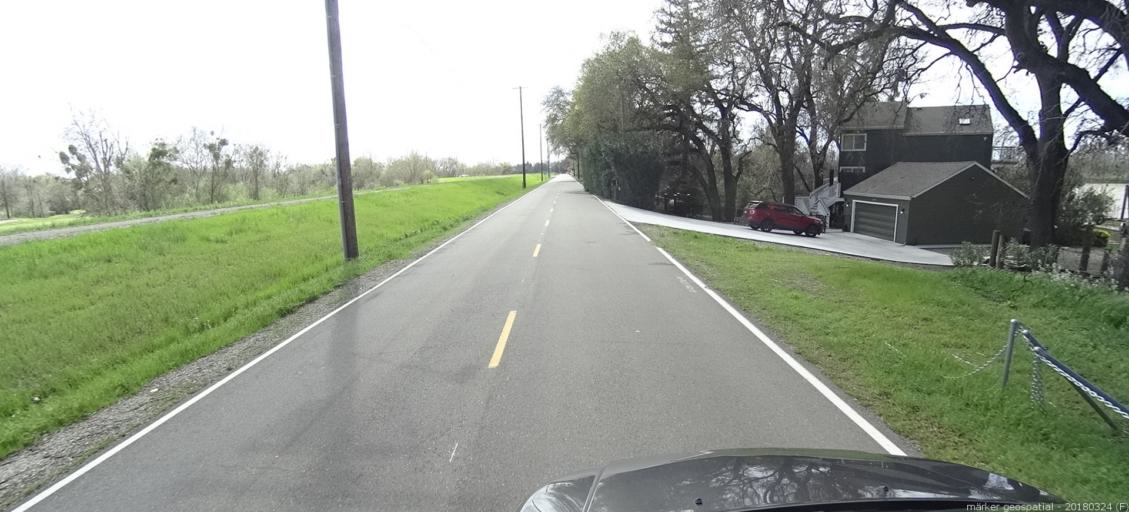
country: US
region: California
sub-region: Yolo County
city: West Sacramento
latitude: 38.7030
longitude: -121.6203
